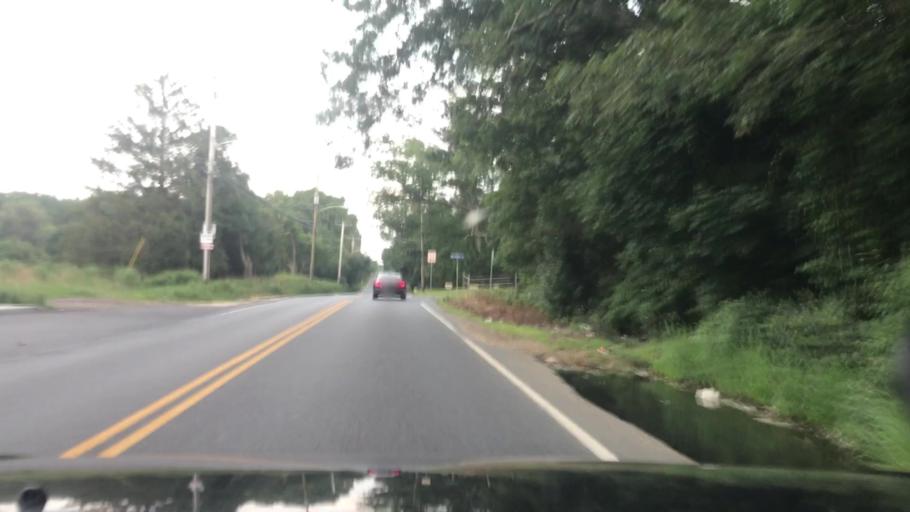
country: US
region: New Jersey
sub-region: Ocean County
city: Lakewood
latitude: 40.0791
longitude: -74.2541
